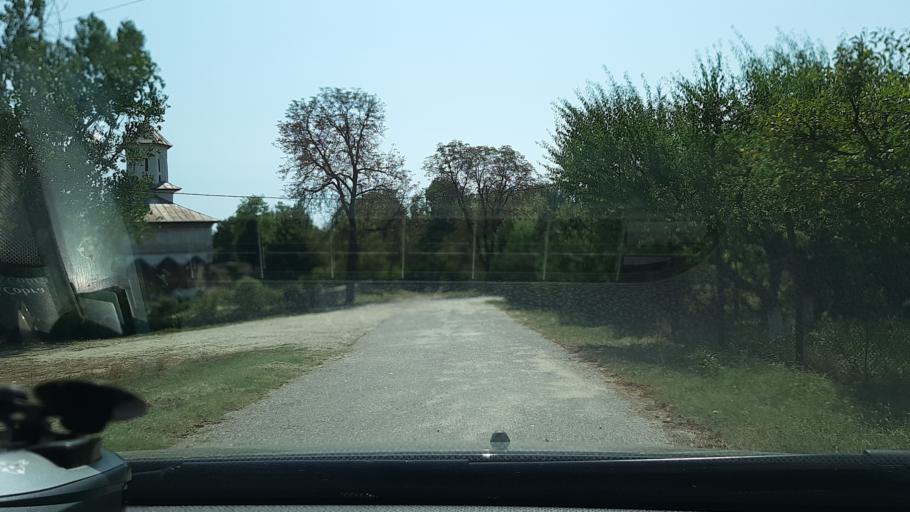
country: RO
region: Gorj
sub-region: Comuna Targu Carbunesti
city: Targu Carbunesti
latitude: 44.9628
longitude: 23.5211
